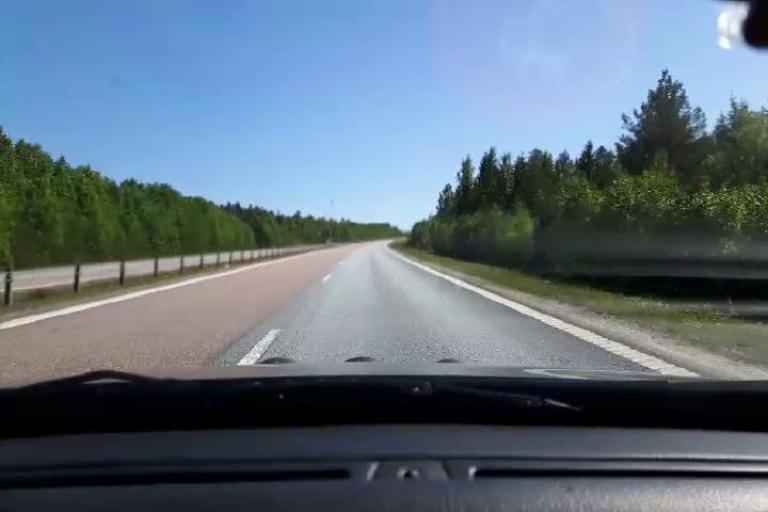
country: SE
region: Gaevleborg
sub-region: Hudiksvalls Kommun
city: Iggesund
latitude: 61.5122
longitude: 16.9843
